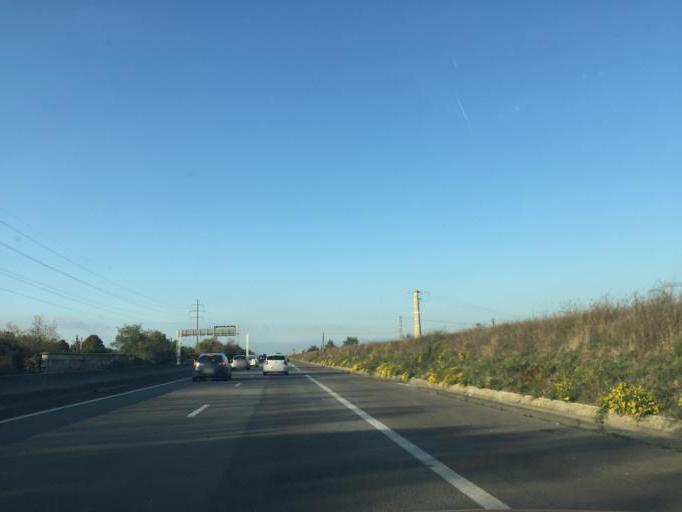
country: FR
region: Rhone-Alpes
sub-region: Departement de la Drome
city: Malissard
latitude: 44.9308
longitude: 4.9454
